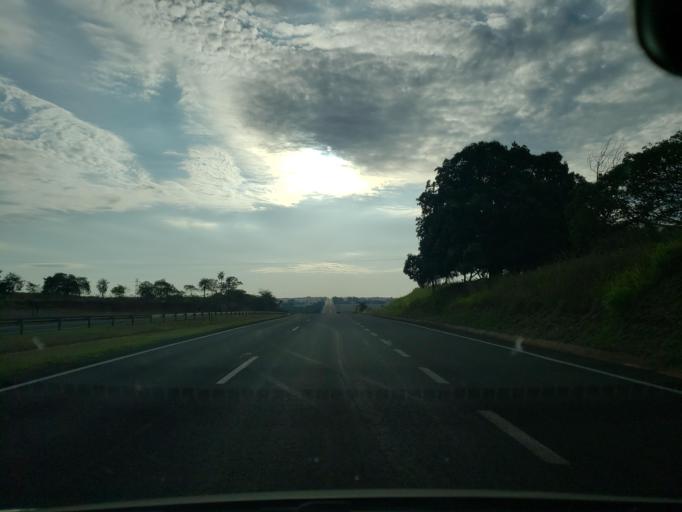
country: BR
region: Sao Paulo
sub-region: Mirandopolis
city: Mirandopolis
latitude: -21.0863
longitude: -51.0626
